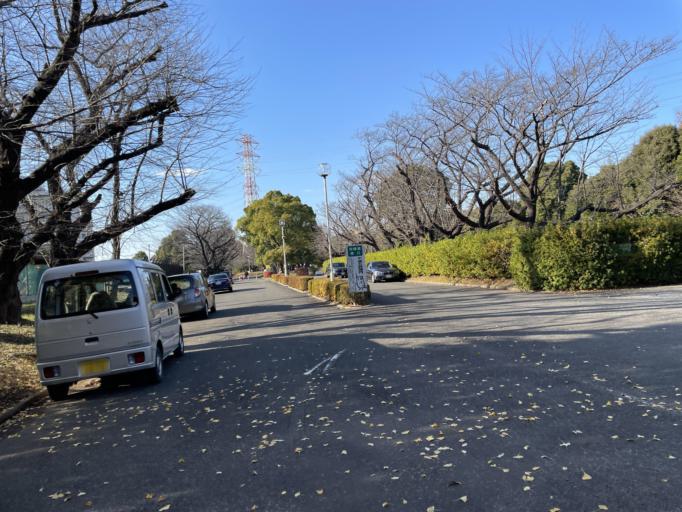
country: JP
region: Saitama
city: Asaka
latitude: 35.7791
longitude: 139.5885
